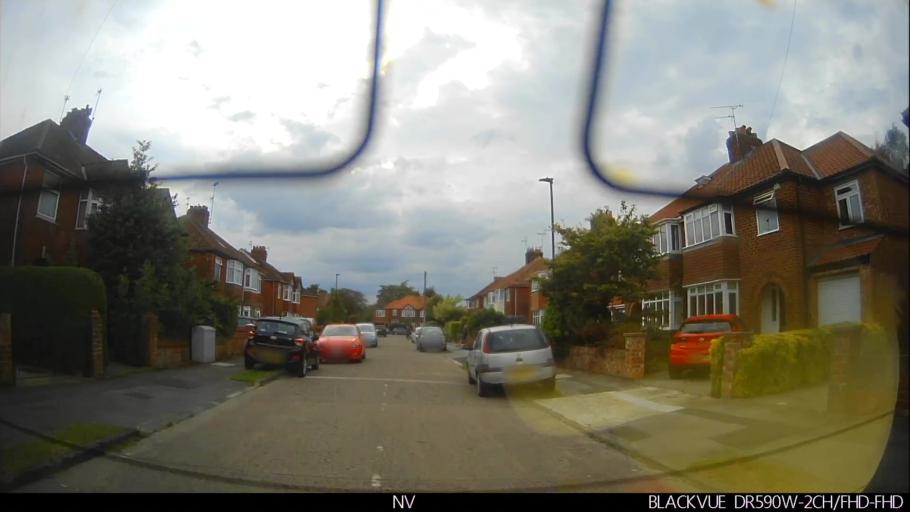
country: GB
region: England
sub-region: City of York
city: Fulford
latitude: 53.9373
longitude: -1.0668
